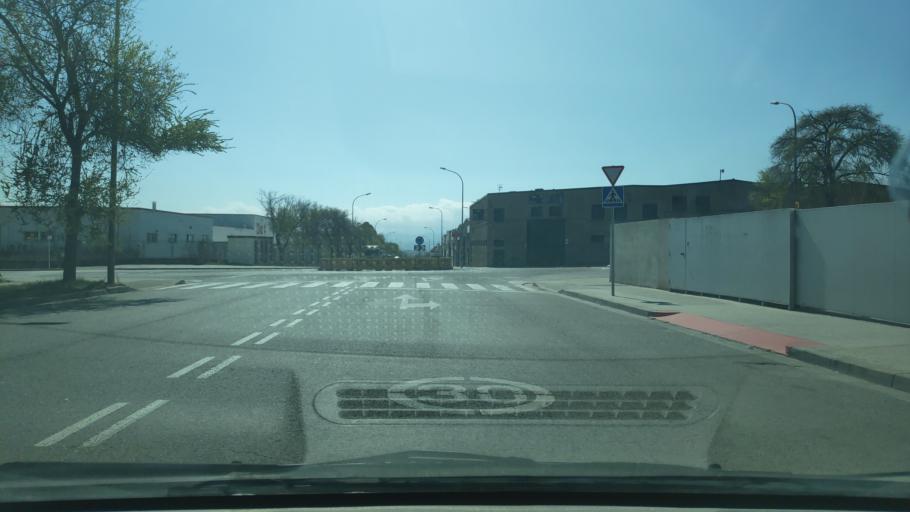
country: ES
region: Catalonia
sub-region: Provincia de Barcelona
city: Polinya
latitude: 41.5378
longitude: 2.1328
